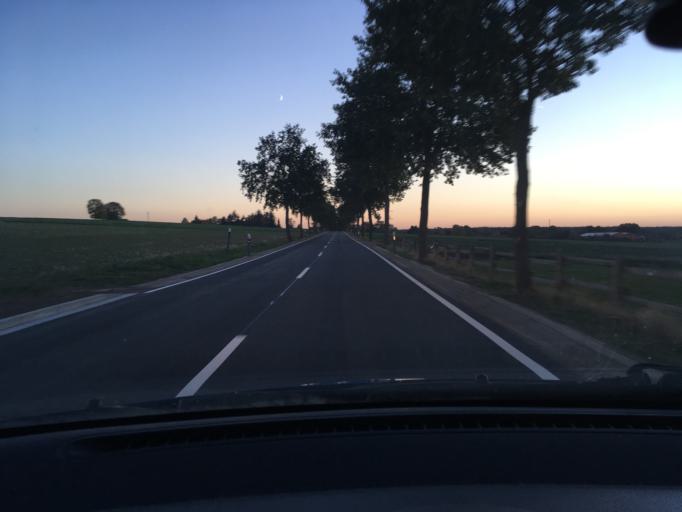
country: DE
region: Lower Saxony
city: Reinstorf
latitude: 53.2396
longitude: 10.5814
